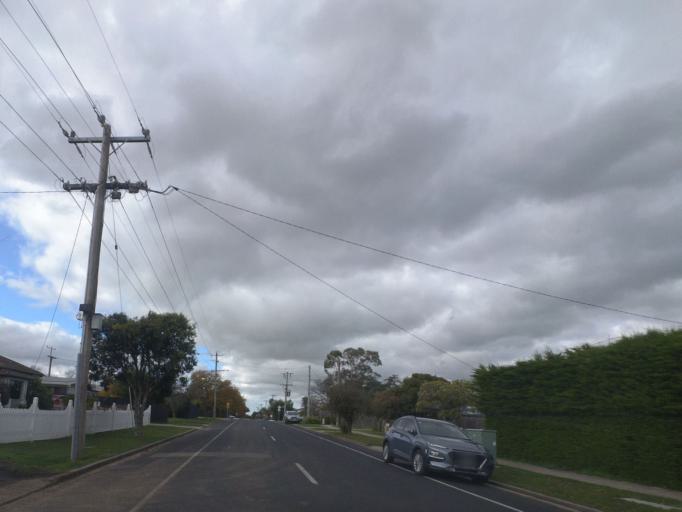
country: AU
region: Victoria
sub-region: Hume
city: Sunbury
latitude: -37.4926
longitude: 144.5949
